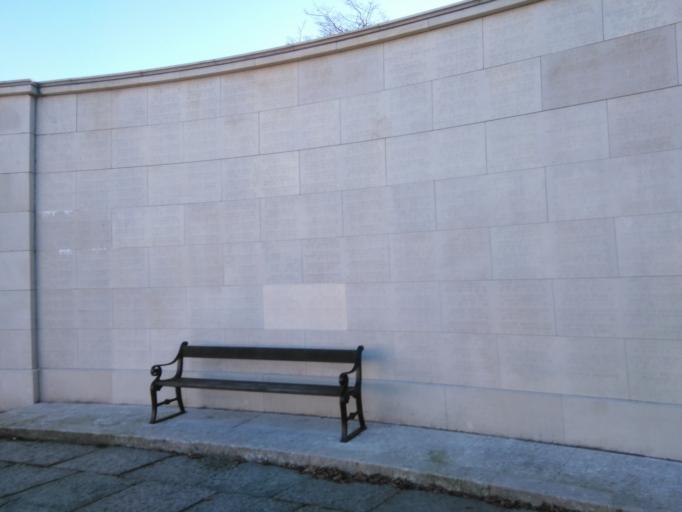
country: DK
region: Central Jutland
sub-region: Arhus Kommune
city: Arhus
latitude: 56.1297
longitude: 10.2084
